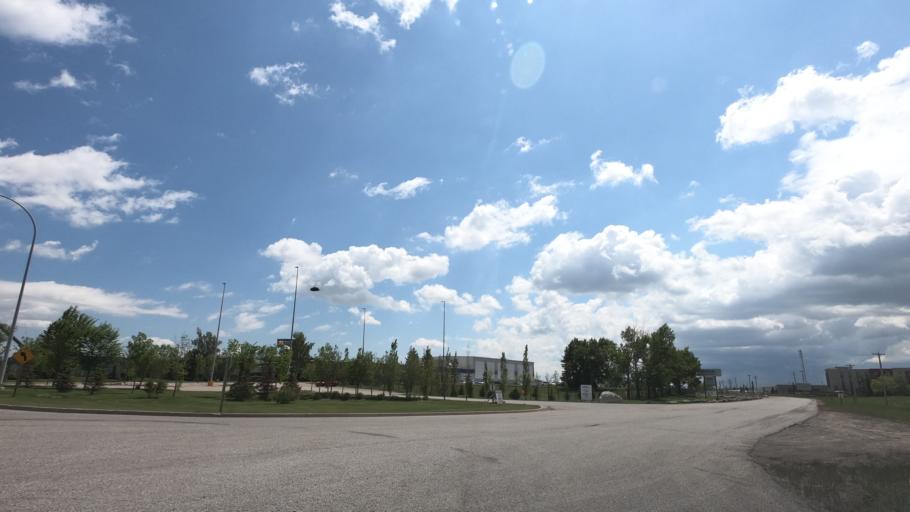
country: CA
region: Alberta
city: Airdrie
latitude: 51.2991
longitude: -113.9963
